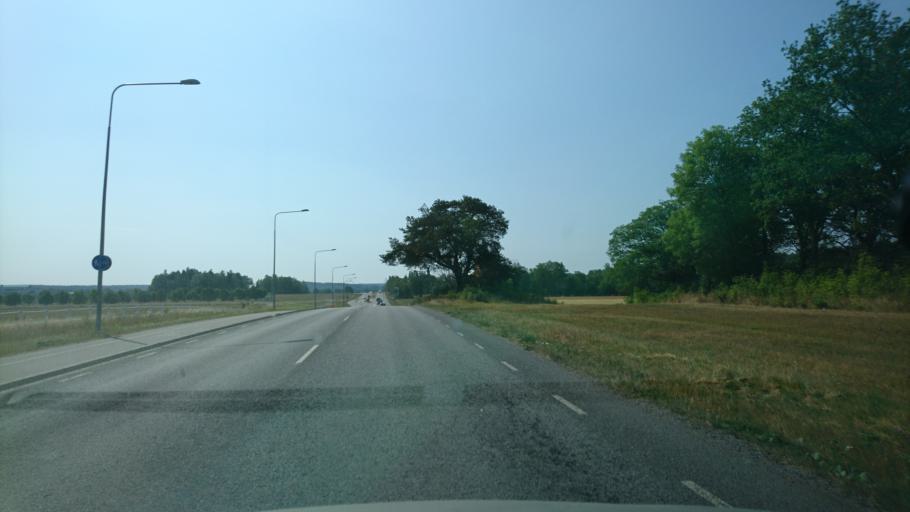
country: SE
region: Uppsala
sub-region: Uppsala Kommun
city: Uppsala
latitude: 59.8212
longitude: 17.6467
